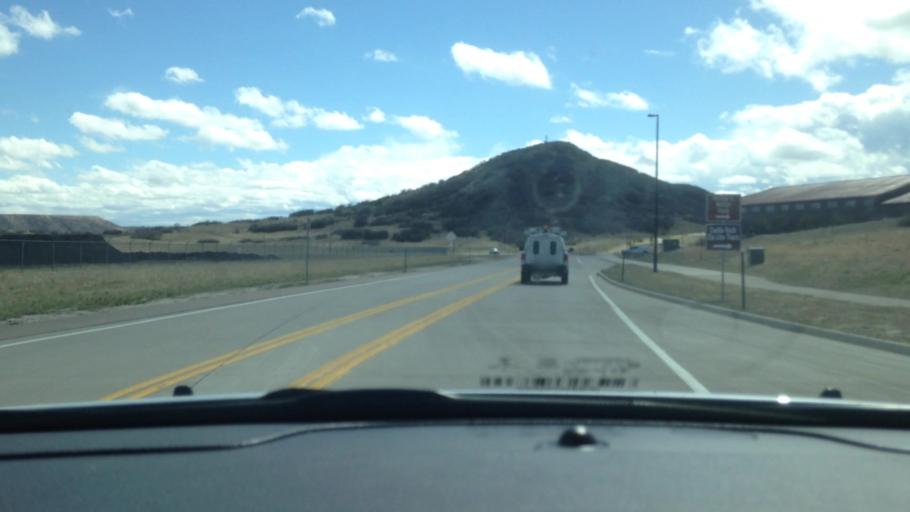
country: US
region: Colorado
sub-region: Douglas County
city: Castle Rock
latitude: 39.3728
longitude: -104.8775
